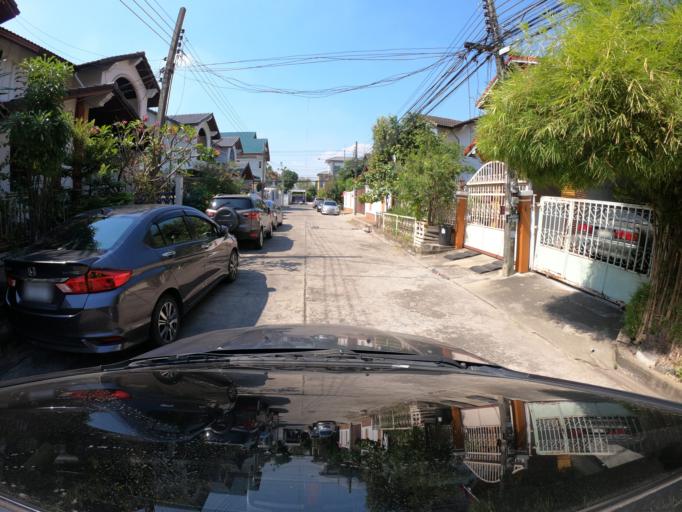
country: TH
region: Bangkok
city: Bang Na
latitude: 13.6665
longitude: 100.6140
